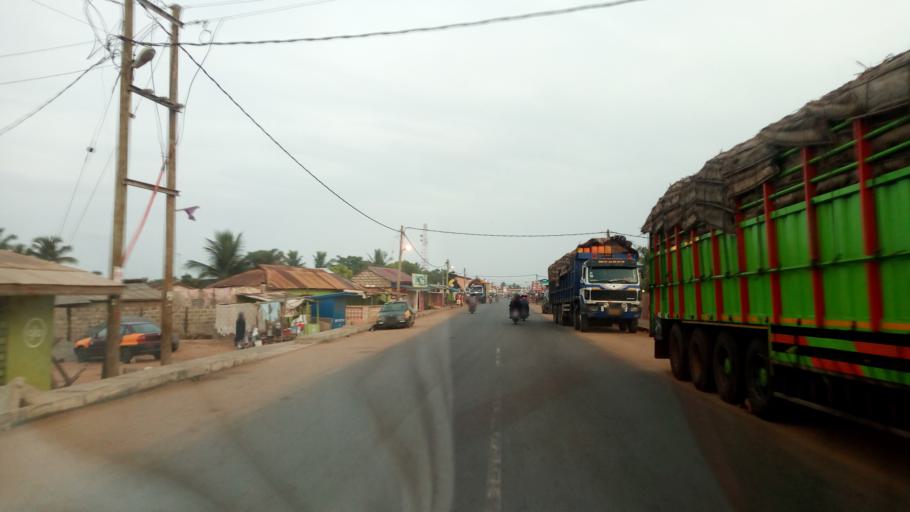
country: TG
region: Maritime
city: Lome
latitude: 6.1155
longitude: 1.1926
